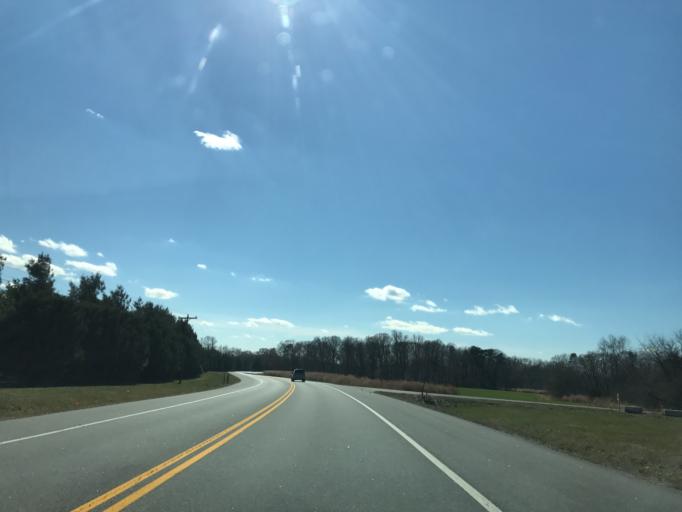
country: US
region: Maryland
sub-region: Queen Anne's County
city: Kingstown
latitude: 39.2407
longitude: -76.0305
